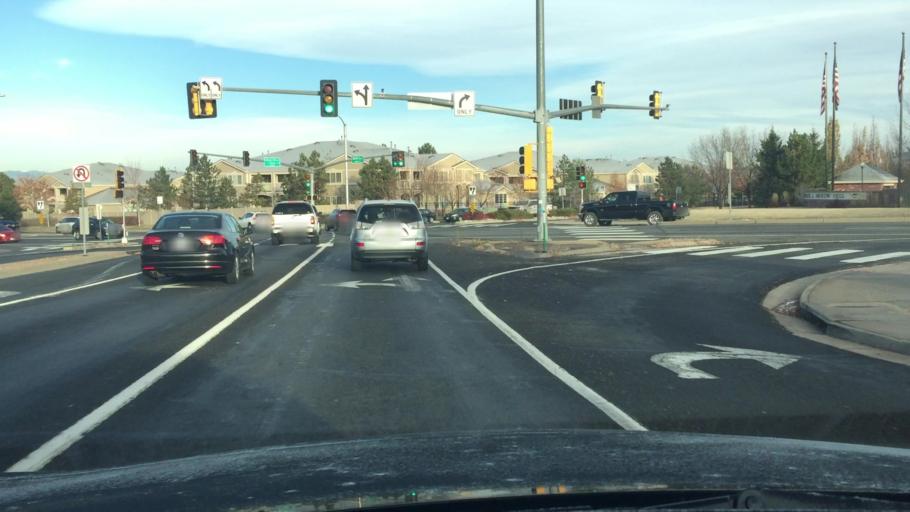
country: US
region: Colorado
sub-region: Arapahoe County
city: Dove Valley
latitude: 39.6382
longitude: -104.8222
